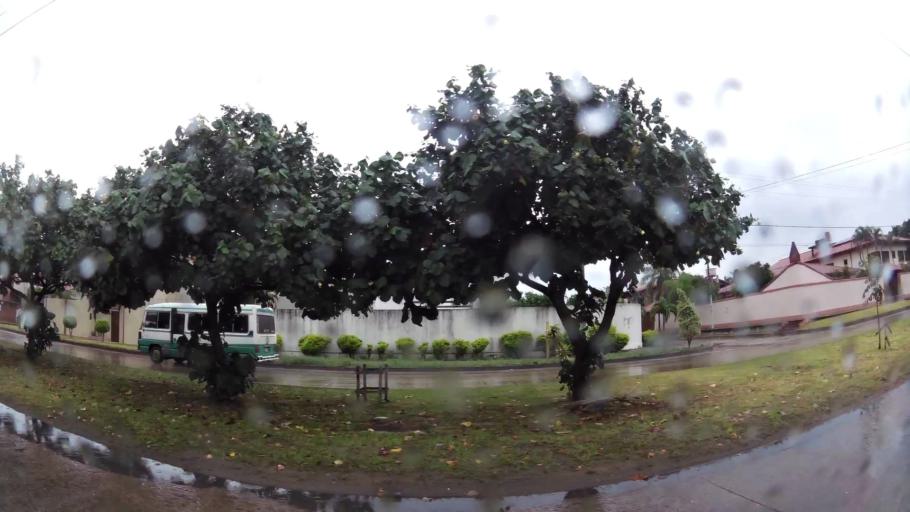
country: BO
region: Santa Cruz
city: Santa Cruz de la Sierra
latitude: -17.8030
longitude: -63.1578
